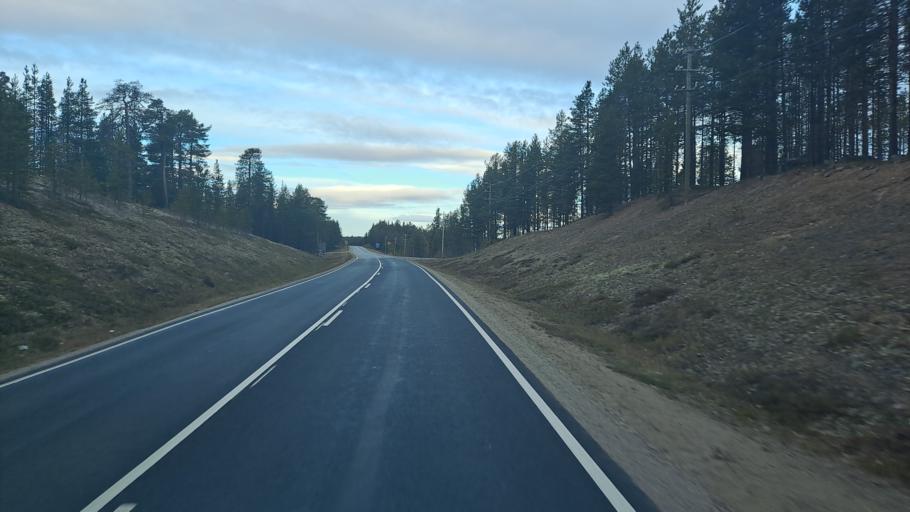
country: FI
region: Lapland
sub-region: Pohjois-Lappi
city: Inari
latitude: 68.9136
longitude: 27.0003
